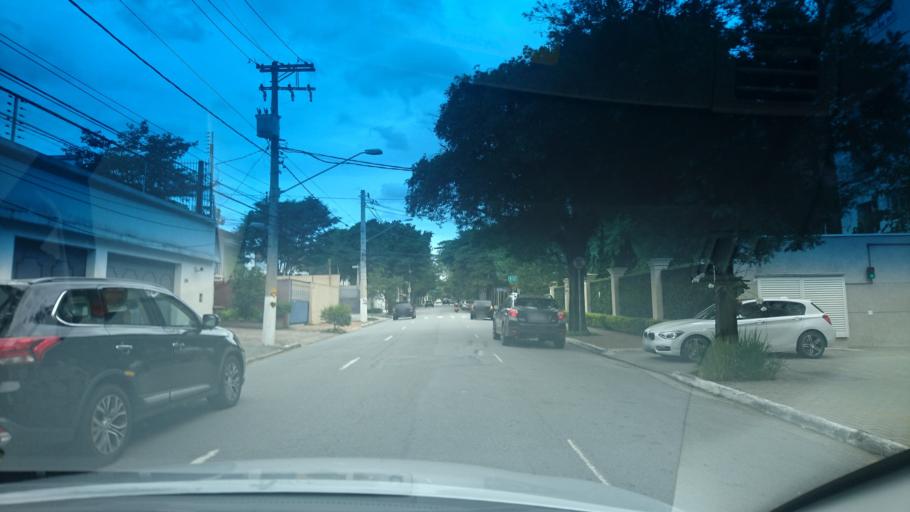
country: BR
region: Sao Paulo
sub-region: Sao Paulo
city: Sao Paulo
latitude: -23.5776
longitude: -46.6698
